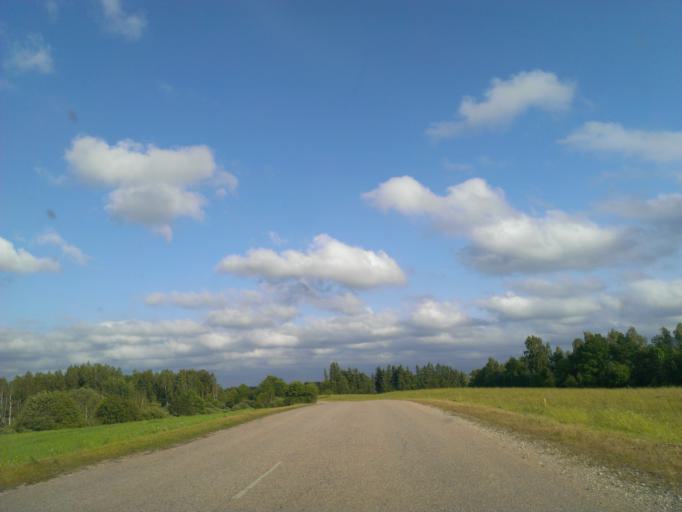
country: LV
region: Aizpute
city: Aizpute
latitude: 56.7538
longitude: 21.5610
